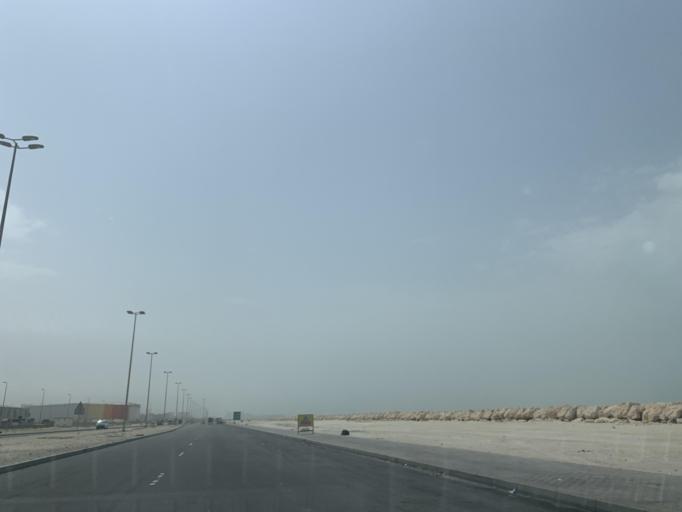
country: BH
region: Muharraq
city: Al Hadd
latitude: 26.2255
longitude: 50.6921
